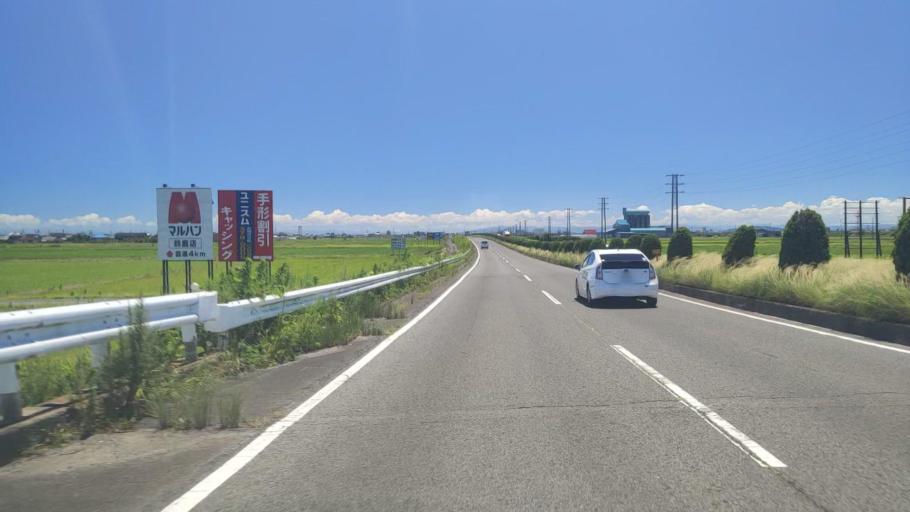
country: JP
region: Mie
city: Suzuka
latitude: 34.8921
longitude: 136.6010
